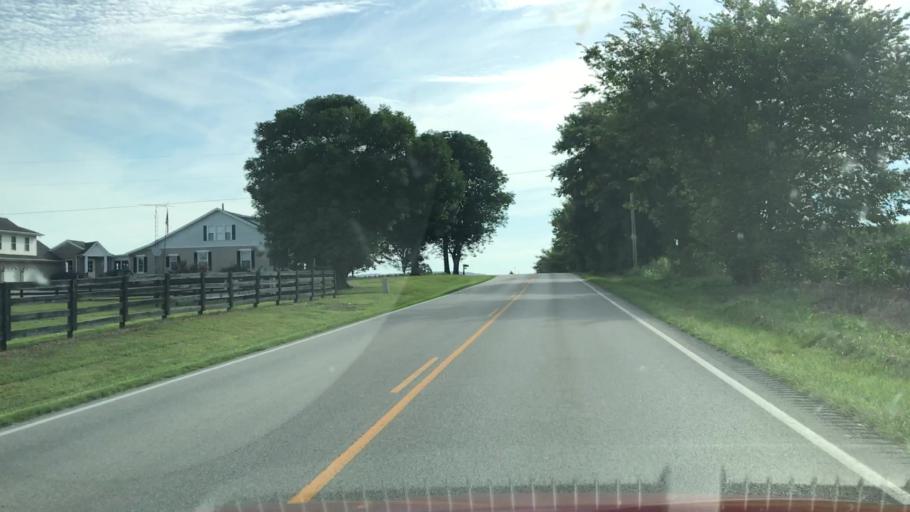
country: US
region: Kentucky
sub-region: Edmonson County
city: Brownsville
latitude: 37.0805
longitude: -86.2407
